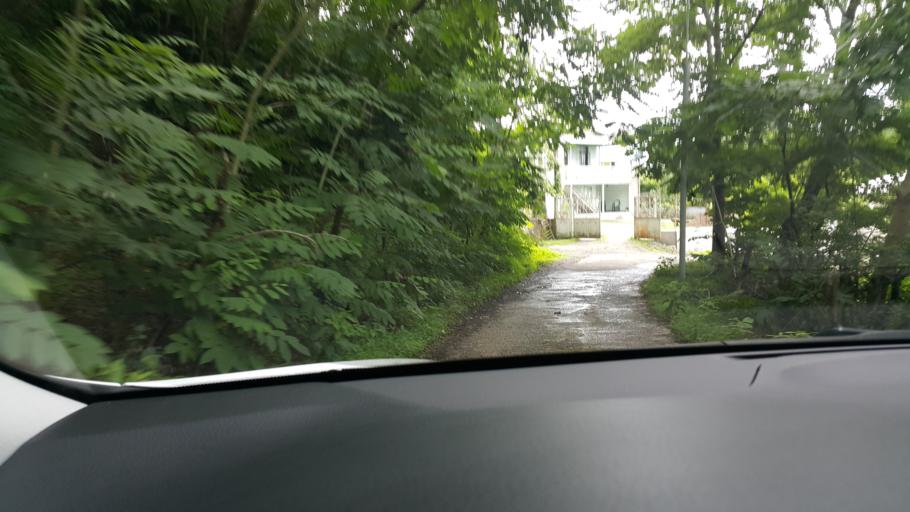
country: GE
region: Ajaria
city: Khelvachauri
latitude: 41.6129
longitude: 41.6550
